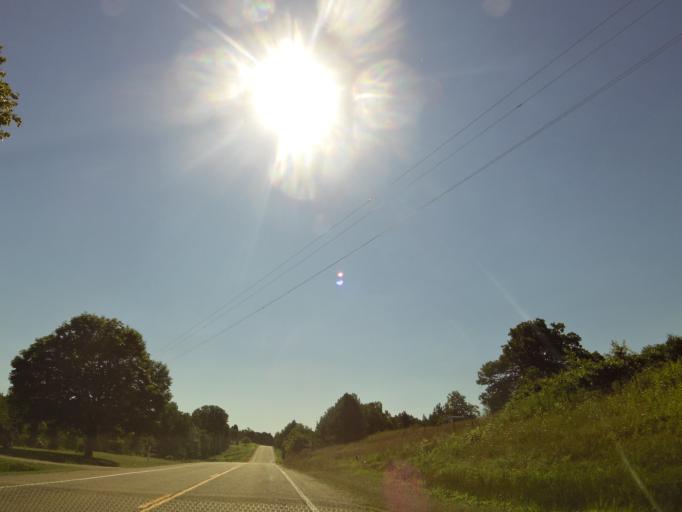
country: US
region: Arkansas
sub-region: Clay County
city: Piggott
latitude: 36.4337
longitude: -90.3316
